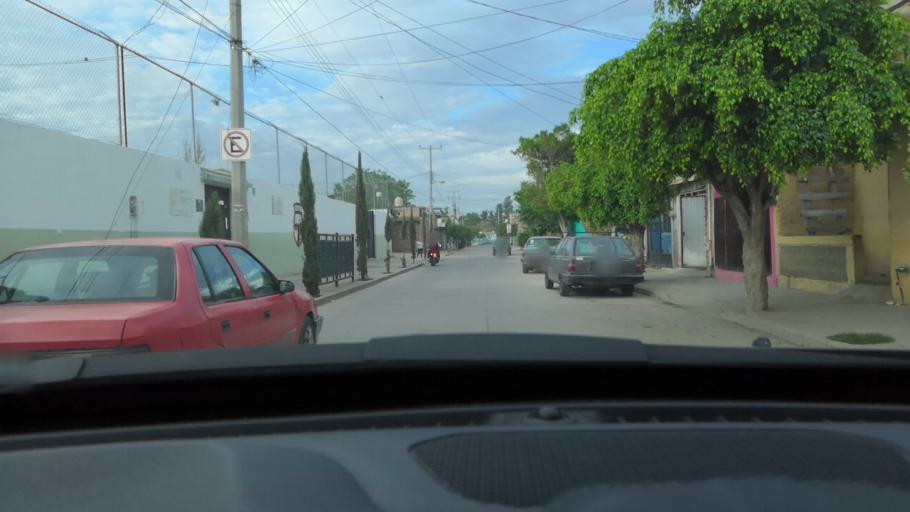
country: MX
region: Guanajuato
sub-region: Leon
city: Fraccionamiento Paraiso Real
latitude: 21.0938
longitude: -101.6046
